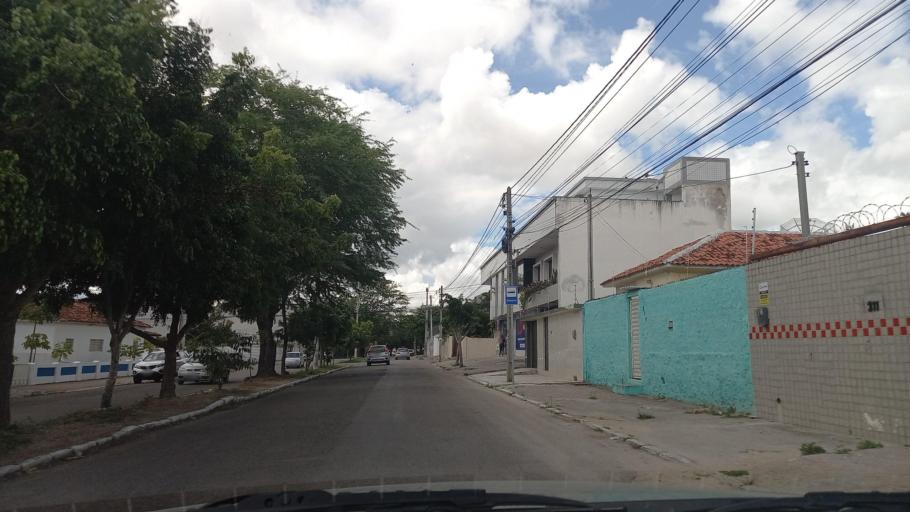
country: BR
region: Pernambuco
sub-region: Caruaru
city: Caruaru
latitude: -8.2967
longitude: -35.9758
